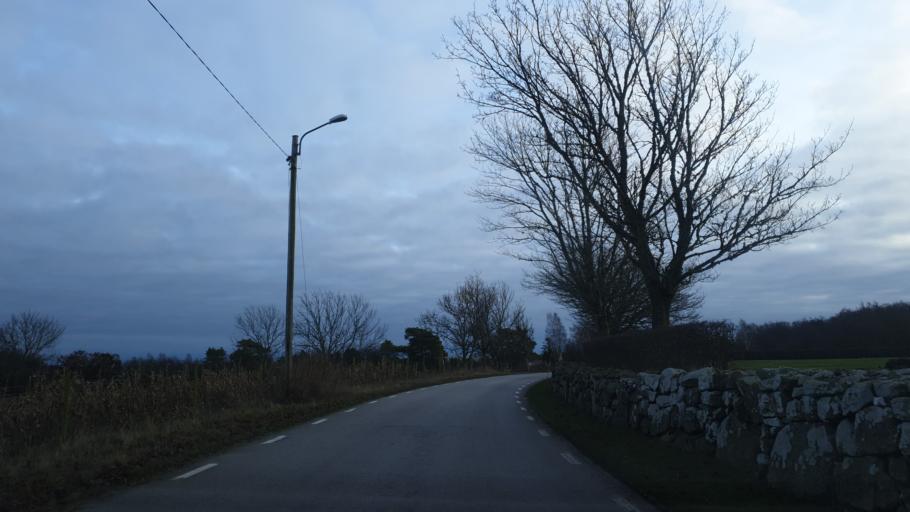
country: SE
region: Kalmar
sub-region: Torsas Kommun
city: Torsas
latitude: 56.2636
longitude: 16.0362
